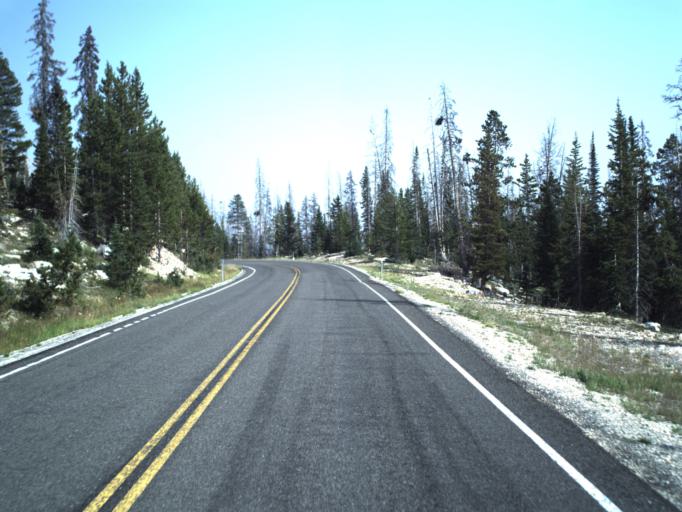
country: US
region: Utah
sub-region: Summit County
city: Kamas
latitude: 40.7123
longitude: -110.8838
